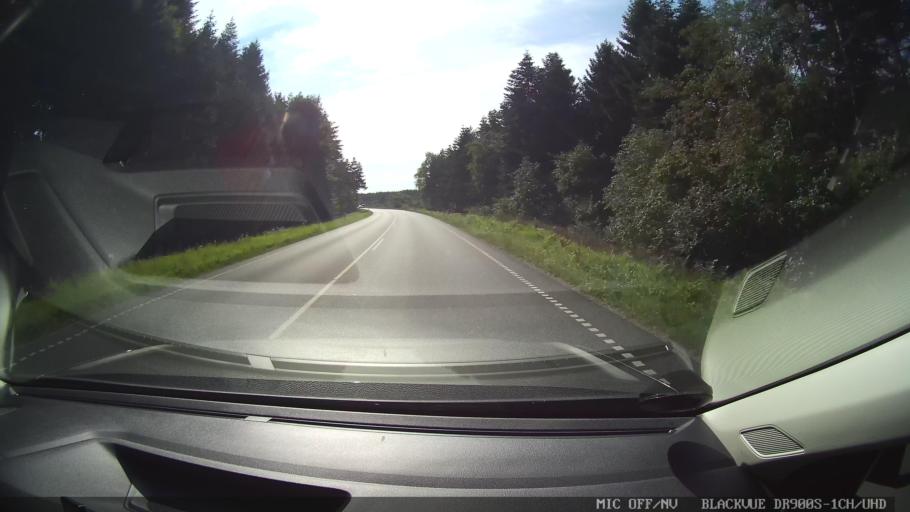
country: DK
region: North Denmark
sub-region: Mariagerfjord Kommune
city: Hadsund
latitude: 56.7328
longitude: 10.0806
